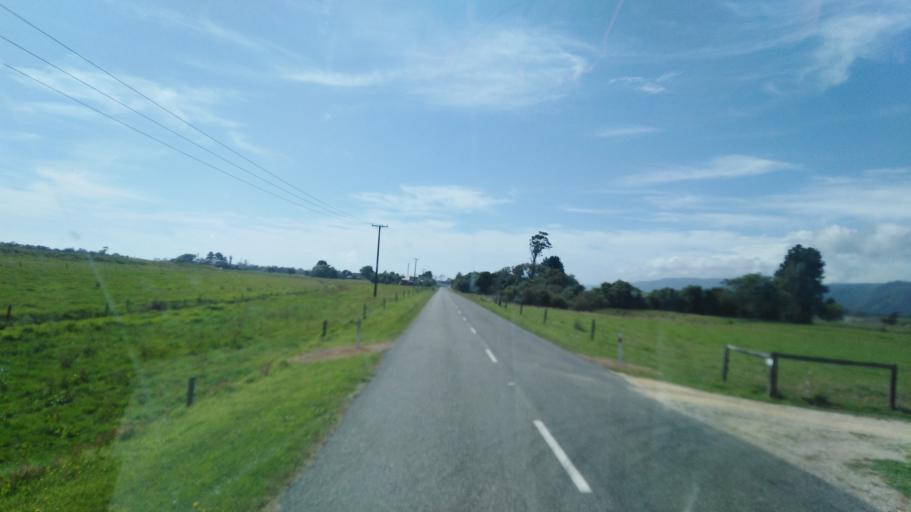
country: NZ
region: West Coast
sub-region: Buller District
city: Westport
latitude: -41.2568
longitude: 172.1311
